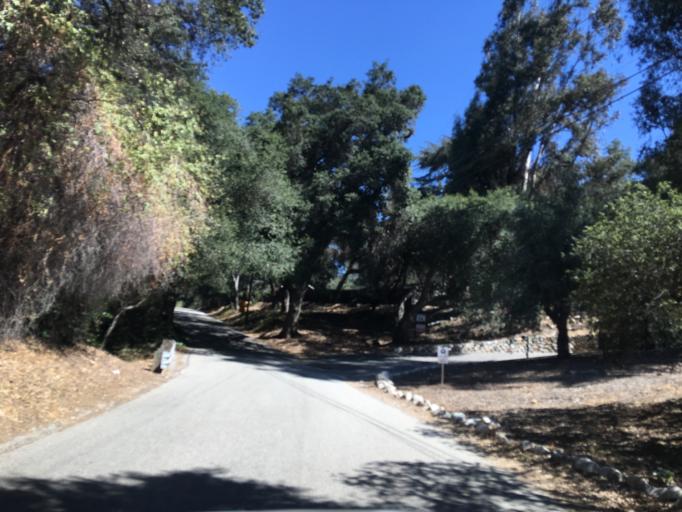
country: US
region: California
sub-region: Los Angeles County
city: Claremont
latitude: 34.1243
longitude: -117.7407
